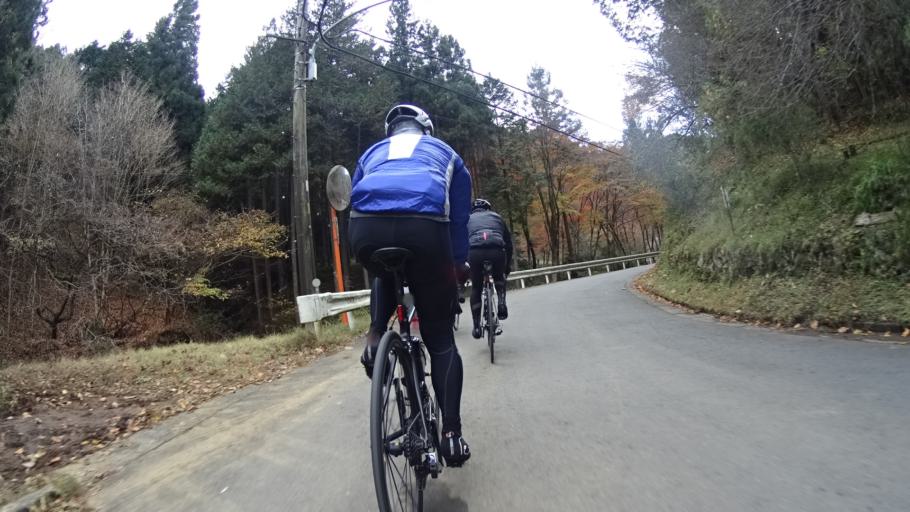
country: JP
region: Saitama
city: Morohongo
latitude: 35.9204
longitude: 139.1870
